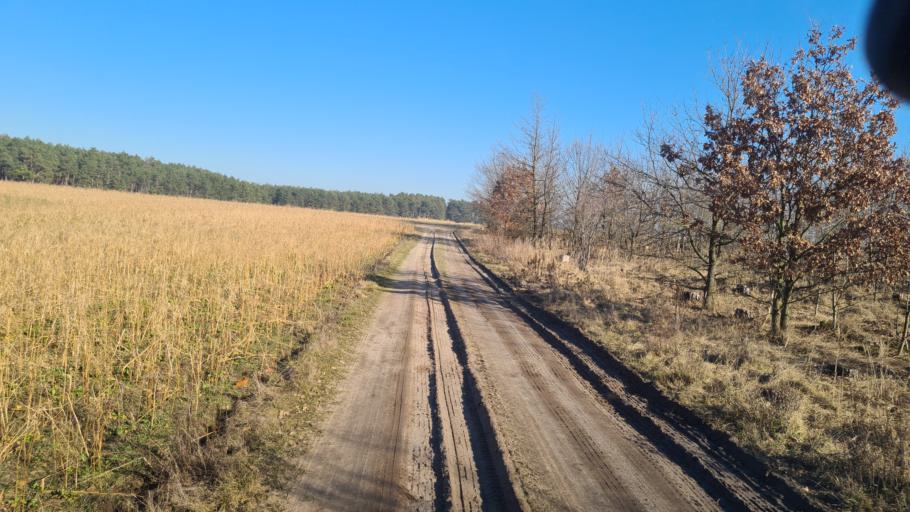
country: DE
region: Brandenburg
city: Hohenbucko
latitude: 51.7156
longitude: 13.4950
